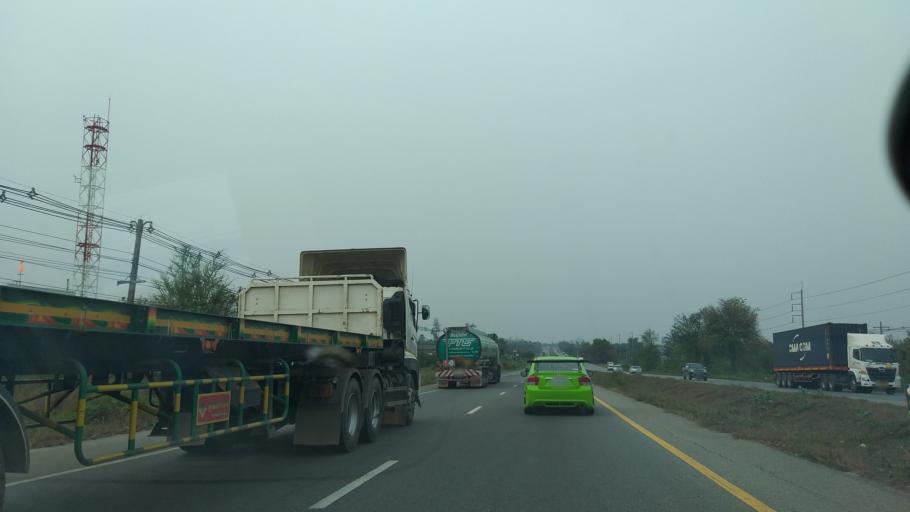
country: TH
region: Chon Buri
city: Ko Chan
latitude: 13.3335
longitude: 101.2703
